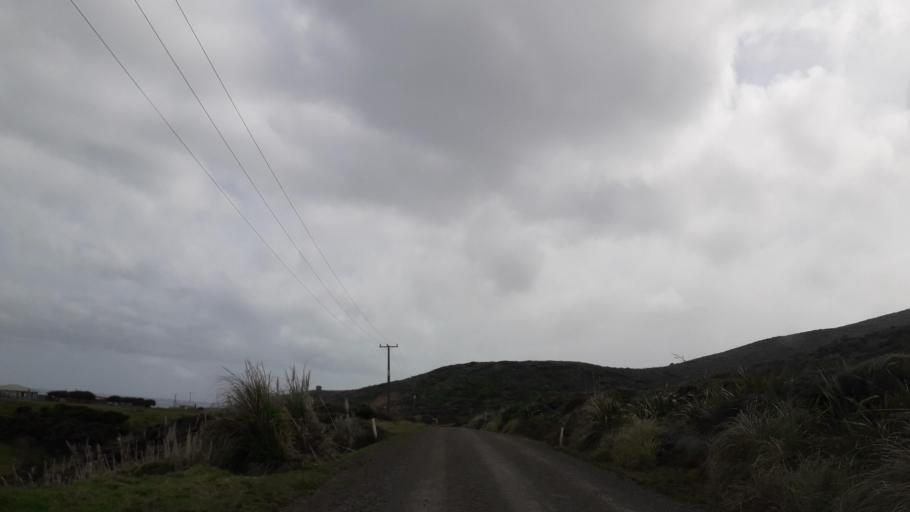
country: NZ
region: Northland
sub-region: Far North District
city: Ahipara
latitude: -35.4320
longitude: 173.2786
